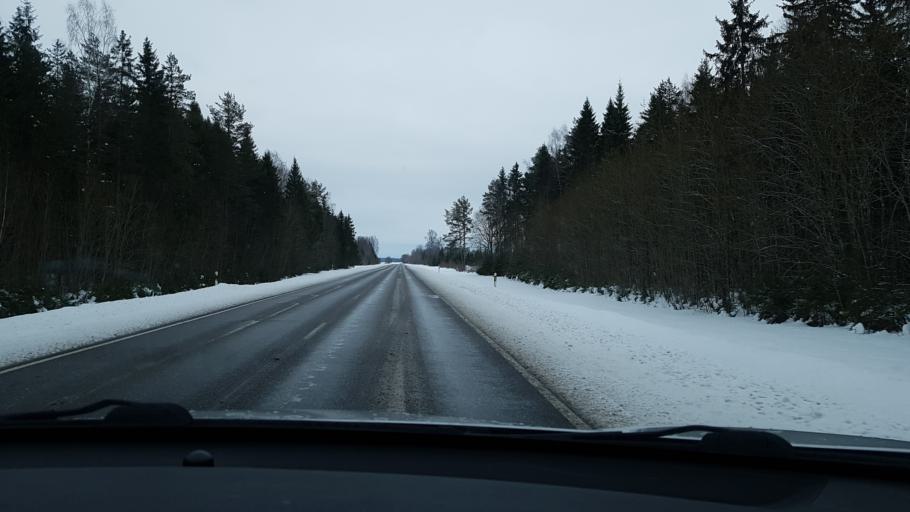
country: EE
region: Jaervamaa
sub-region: Jaerva-Jaani vald
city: Jarva-Jaani
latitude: 59.1322
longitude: 25.7775
